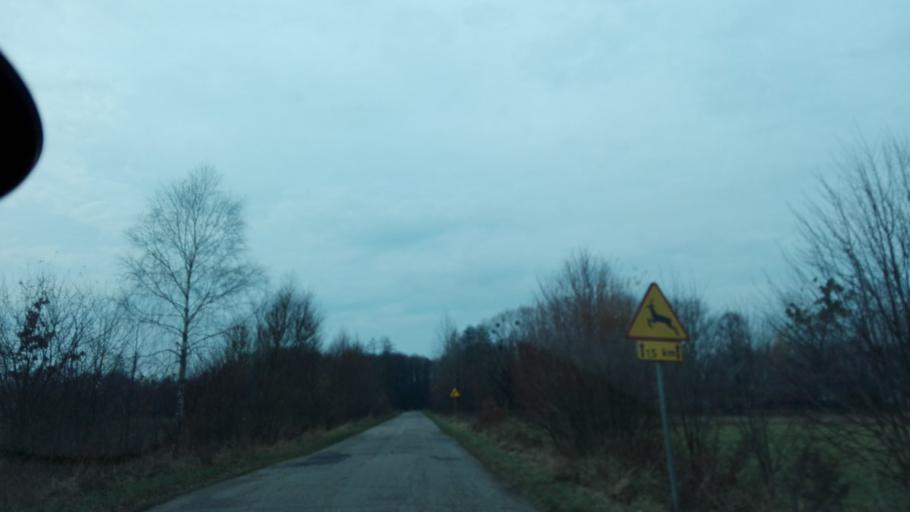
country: PL
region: Lublin Voivodeship
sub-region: Powiat bialski
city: Sosnowka
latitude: 51.7300
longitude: 23.4208
